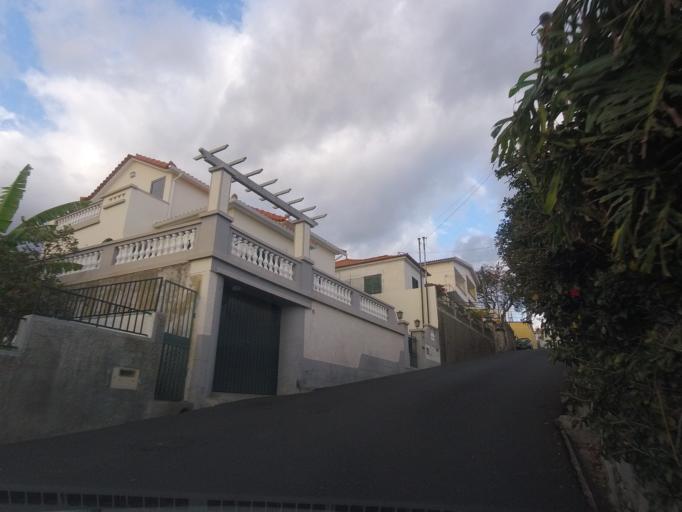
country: PT
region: Madeira
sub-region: Funchal
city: Nossa Senhora do Monte
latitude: 32.6516
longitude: -16.8921
